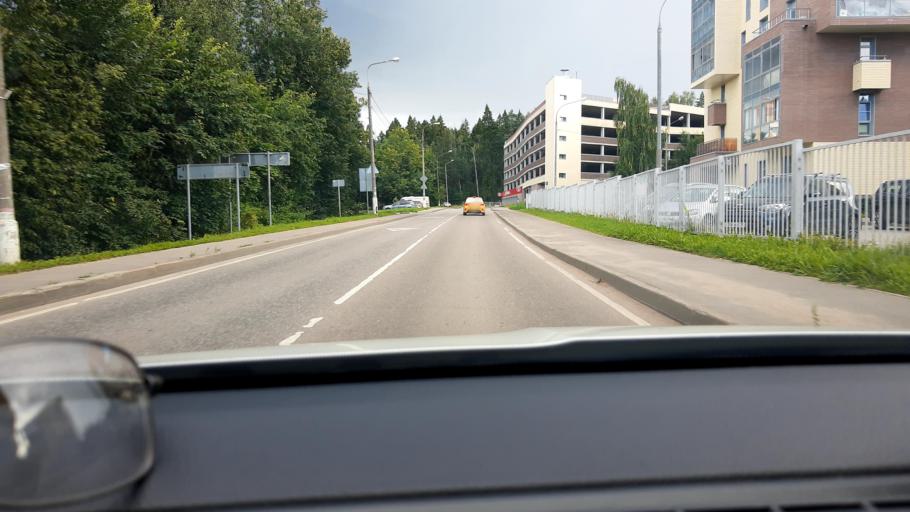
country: RU
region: Moskovskaya
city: Povedniki
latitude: 55.9769
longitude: 37.6064
